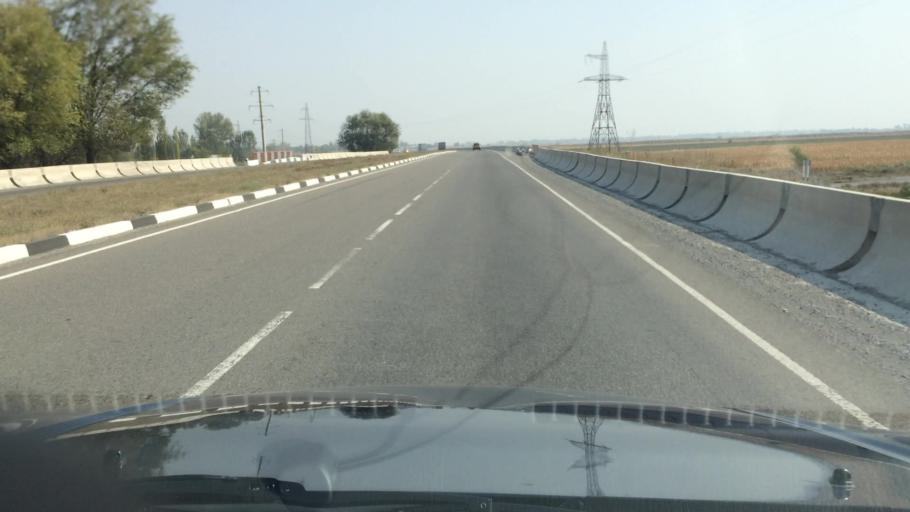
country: KG
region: Chuy
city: Kant
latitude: 42.9672
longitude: 74.8360
